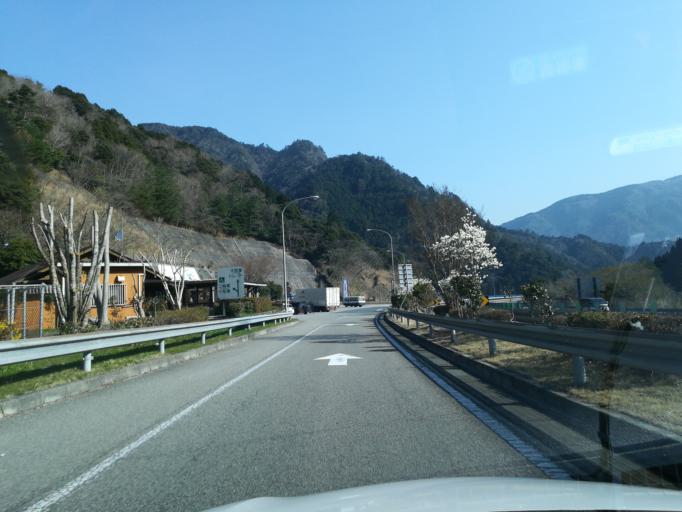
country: JP
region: Ehime
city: Kawanoecho
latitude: 33.9102
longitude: 133.6301
